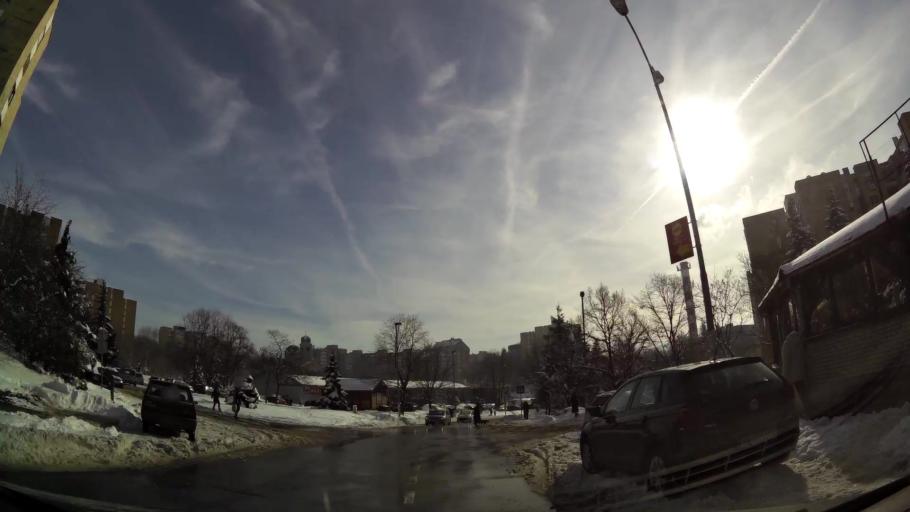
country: RS
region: Central Serbia
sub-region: Belgrade
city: Zvezdara
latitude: 44.7908
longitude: 20.5334
